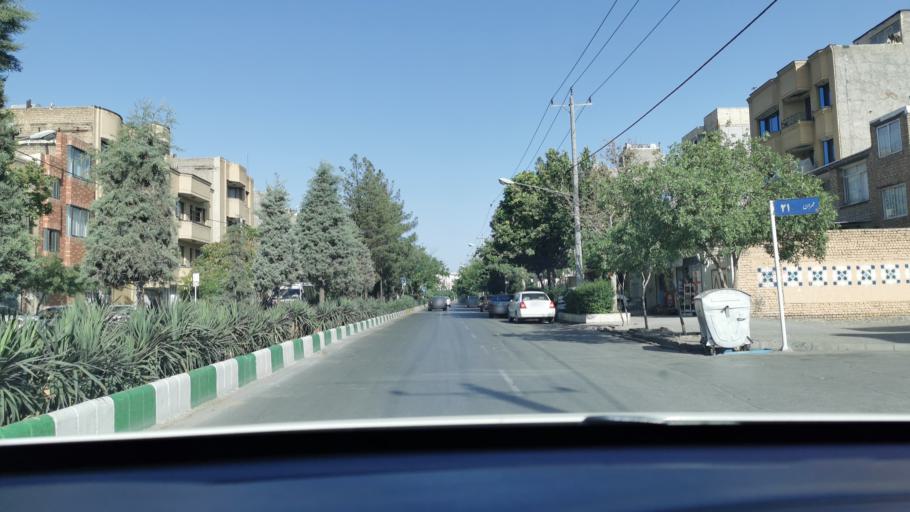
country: IR
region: Razavi Khorasan
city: Mashhad
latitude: 36.3378
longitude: 59.5115
